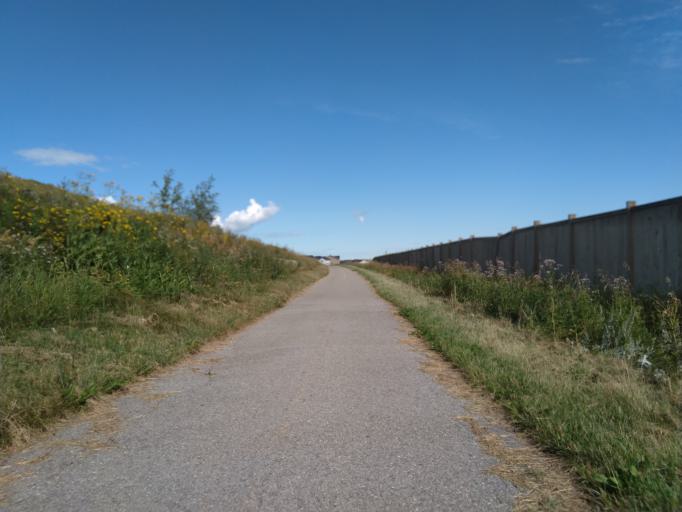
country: CA
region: Alberta
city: Calgary
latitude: 51.1544
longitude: -114.1529
